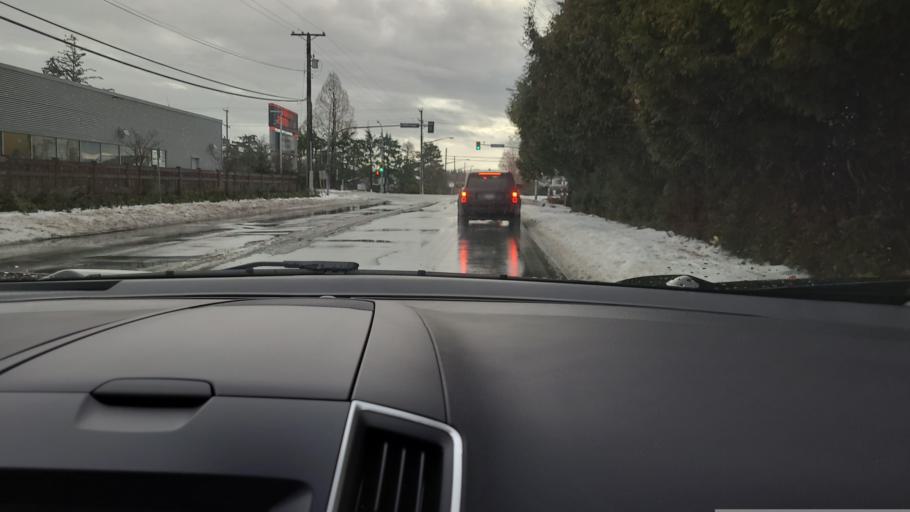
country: CA
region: British Columbia
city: Richmond
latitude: 49.1710
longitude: -123.0804
